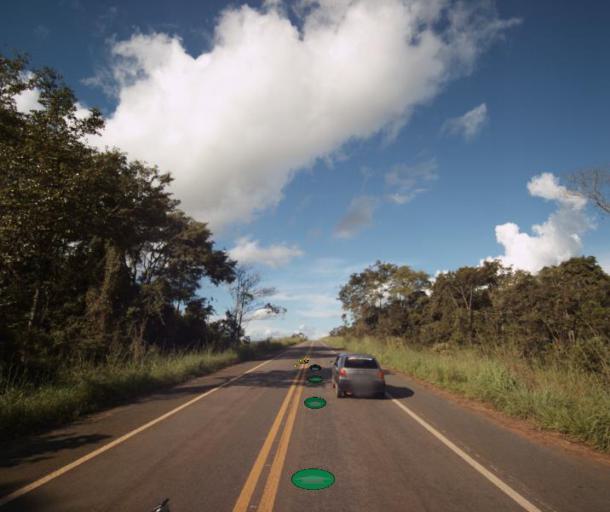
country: BR
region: Goias
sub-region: Itaberai
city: Itaberai
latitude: -15.9966
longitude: -49.7396
